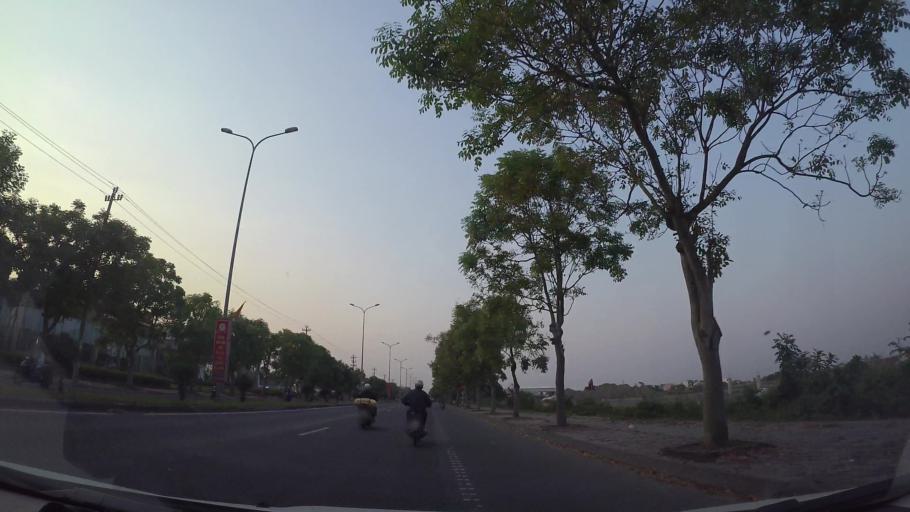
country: VN
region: Da Nang
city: Cam Le
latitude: 15.9631
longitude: 108.2128
